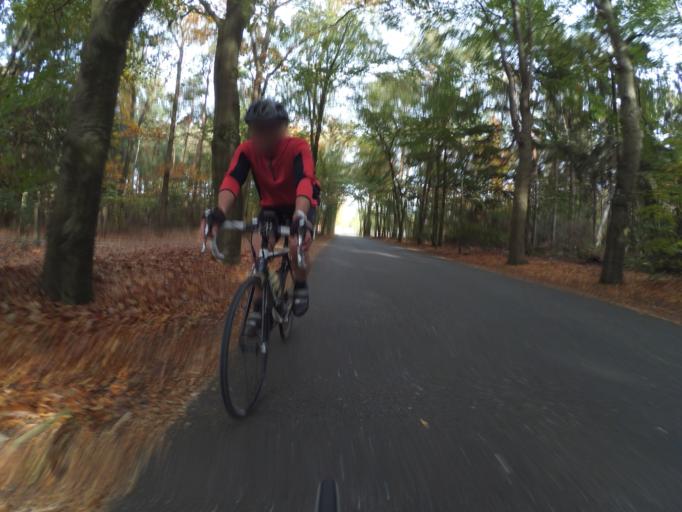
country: NL
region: Overijssel
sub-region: Gemeente Twenterand
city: Den Ham
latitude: 52.3639
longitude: 6.4414
